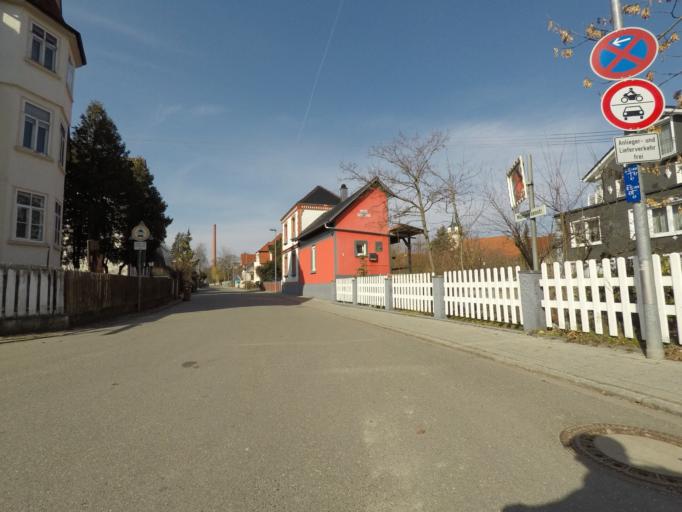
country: DE
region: Baden-Wuerttemberg
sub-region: Tuebingen Region
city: Metzingen
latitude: 48.5346
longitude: 9.2870
